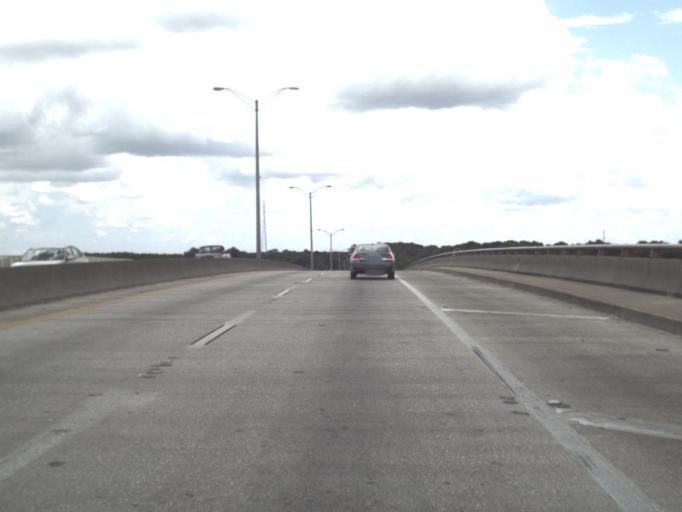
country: US
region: Florida
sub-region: Putnam County
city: Palatka
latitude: 29.6459
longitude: -81.6232
